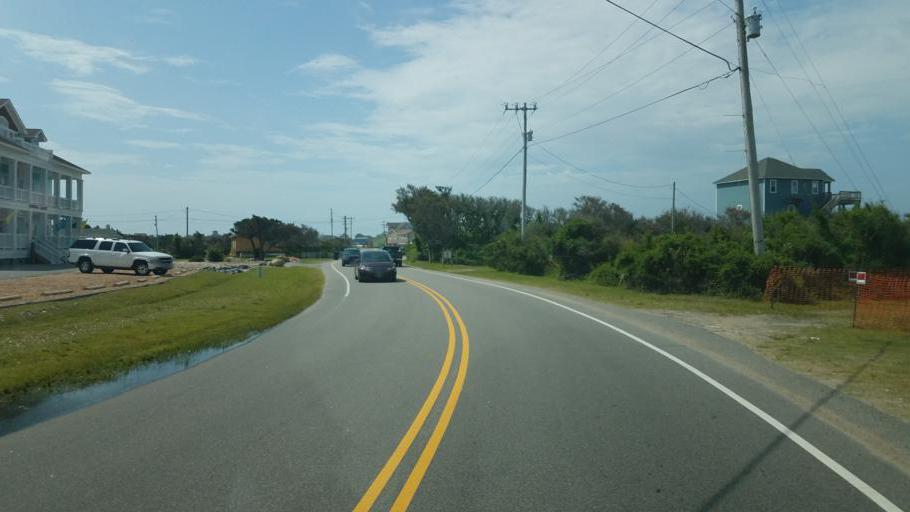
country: US
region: North Carolina
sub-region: Dare County
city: Buxton
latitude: 35.2142
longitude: -75.6994
